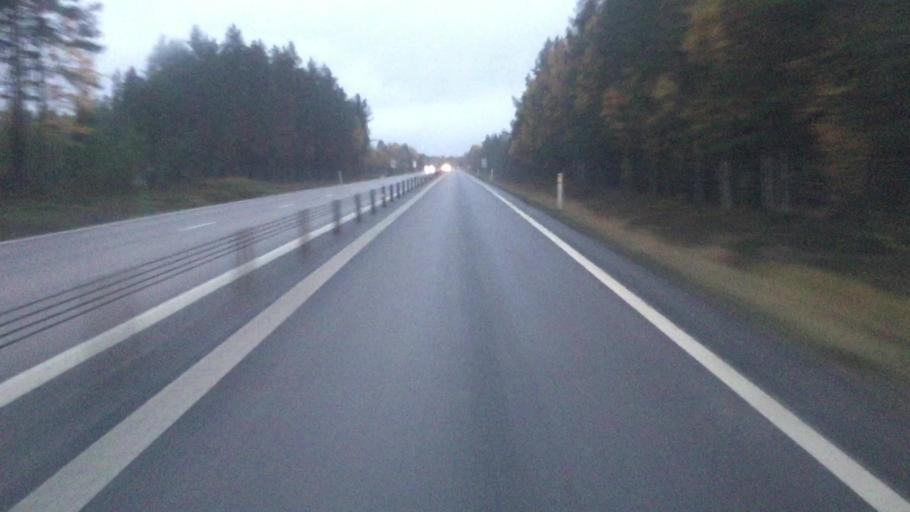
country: SE
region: Vaesterbotten
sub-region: Umea Kommun
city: Saevar
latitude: 63.9765
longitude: 20.7201
